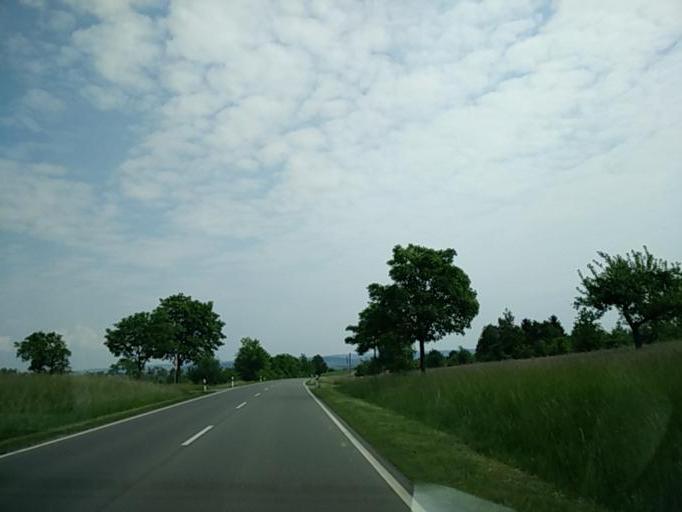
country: DE
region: Baden-Wuerttemberg
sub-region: Tuebingen Region
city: Rottenburg
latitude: 48.4535
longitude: 8.9215
